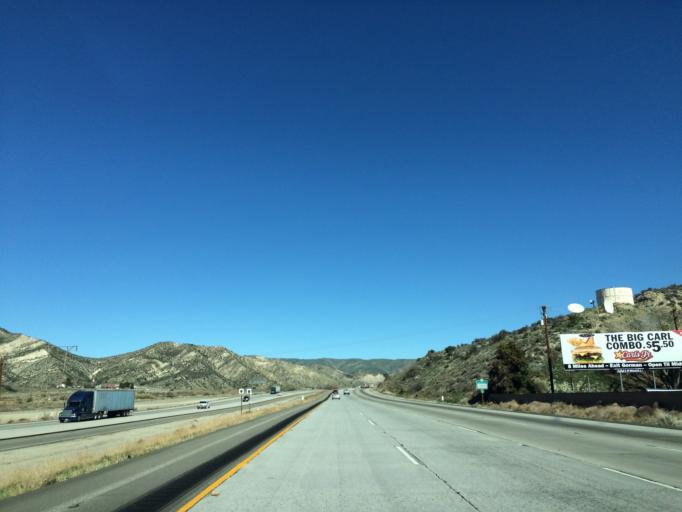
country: US
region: California
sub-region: Kern County
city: Lebec
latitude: 34.7211
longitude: -118.7986
